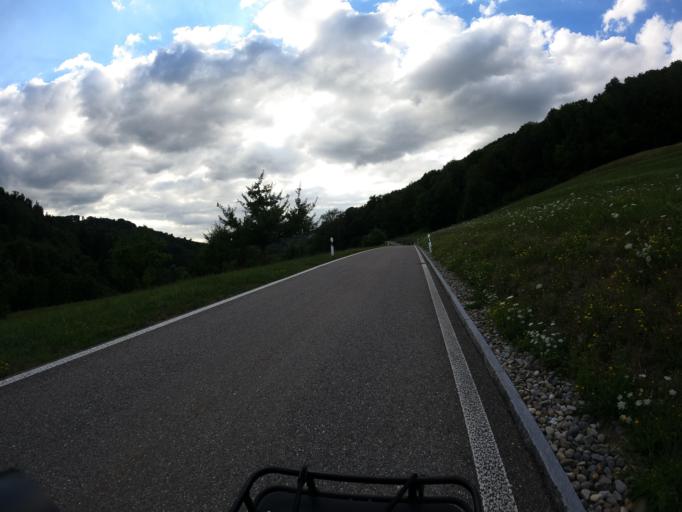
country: CH
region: Zurich
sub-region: Bezirk Dietikon
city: Urdorf / Oberurdorf
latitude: 47.3748
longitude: 8.4083
